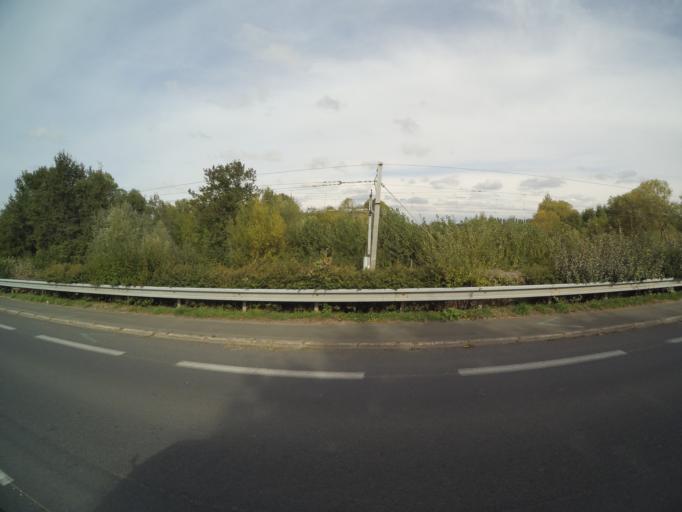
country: FR
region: Pays de la Loire
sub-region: Departement de Maine-et-Loire
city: Saumur
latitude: 47.2645
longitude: -0.0614
